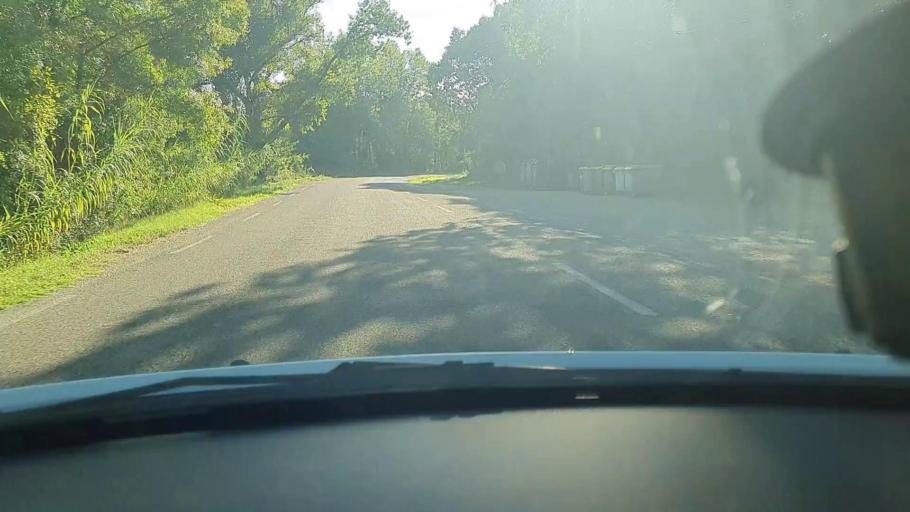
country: FR
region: Languedoc-Roussillon
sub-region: Departement du Gard
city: Goudargues
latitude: 44.2315
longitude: 4.4440
